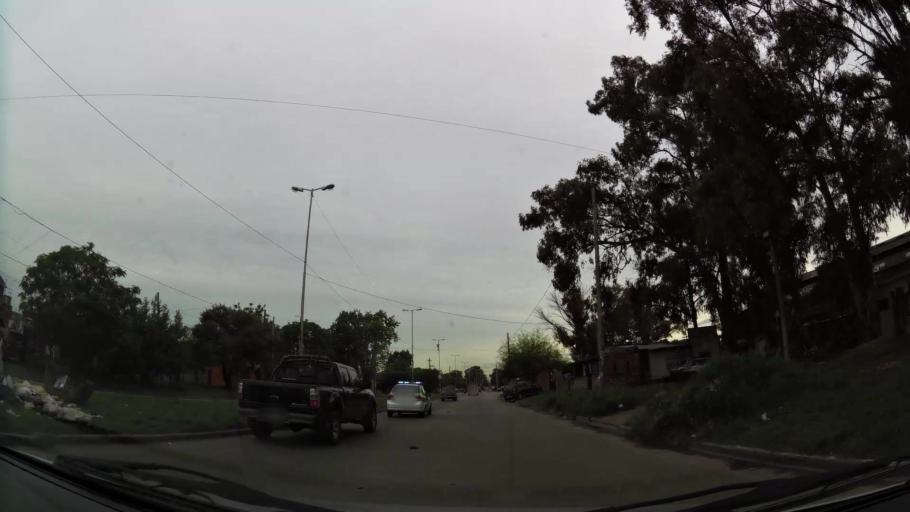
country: AR
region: Buenos Aires
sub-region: Partido de Lanus
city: Lanus
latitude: -34.7192
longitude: -58.3500
